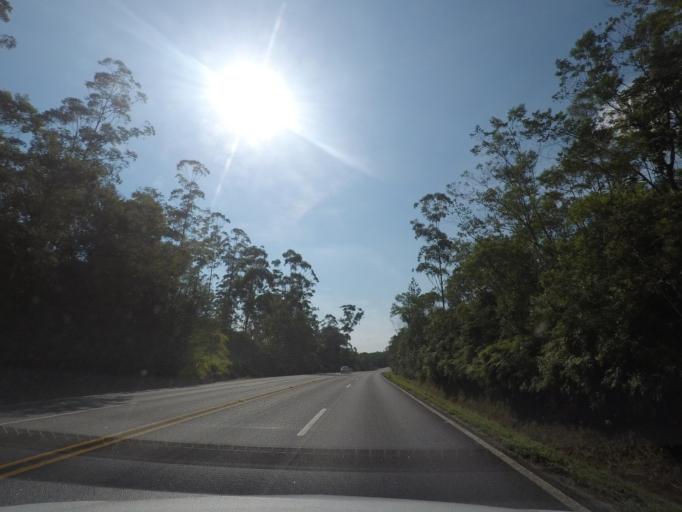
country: BR
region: Parana
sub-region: Paranagua
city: Paranagua
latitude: -25.6007
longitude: -48.6098
